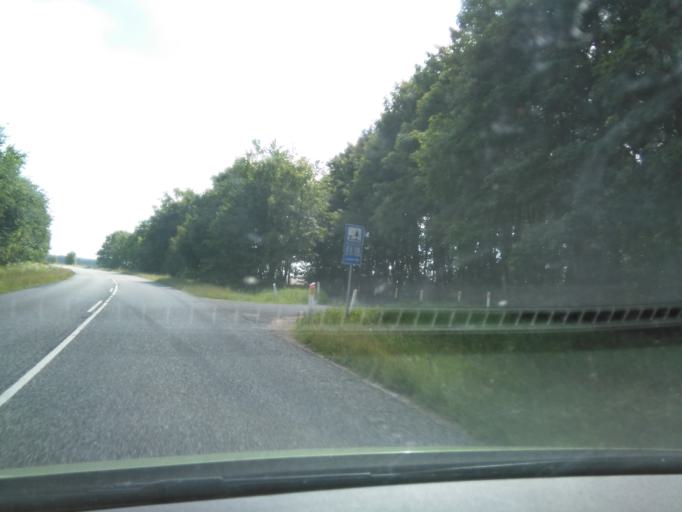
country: DK
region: Central Jutland
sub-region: Odder Kommune
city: Odder
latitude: 55.9669
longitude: 10.0816
